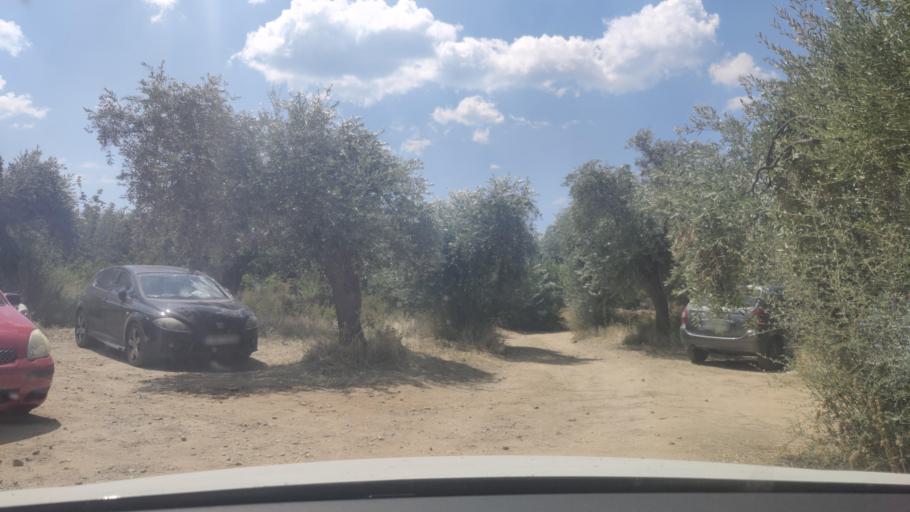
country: GR
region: East Macedonia and Thrace
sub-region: Nomos Kavalas
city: Limenaria
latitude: 40.6377
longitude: 24.5245
